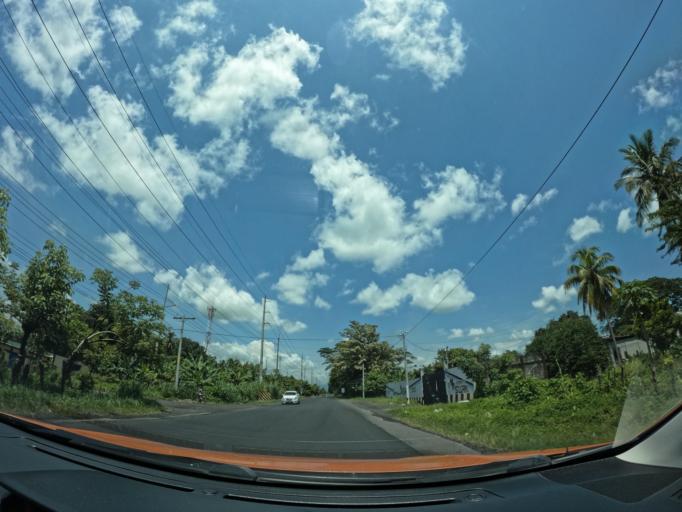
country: GT
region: Escuintla
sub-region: Municipio de Masagua
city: Masagua
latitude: 14.2245
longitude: -90.8289
